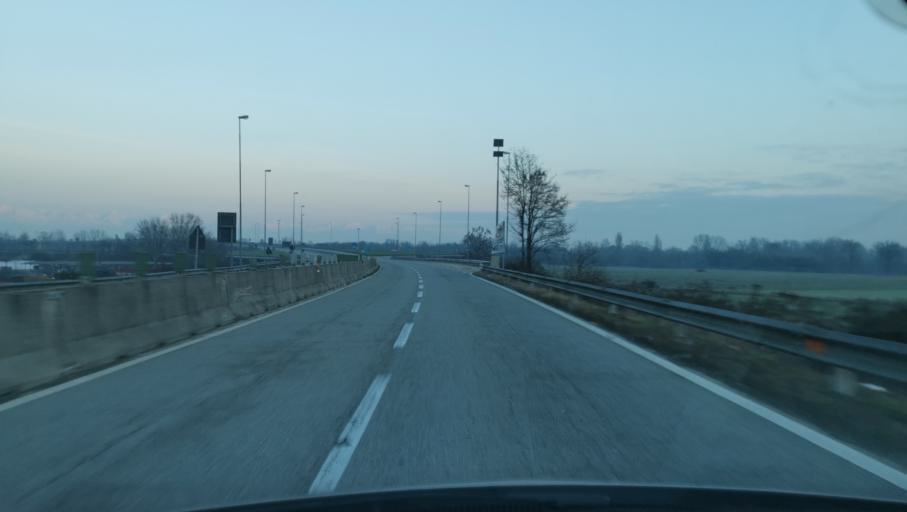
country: IT
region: Piedmont
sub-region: Provincia di Torino
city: Brandizzo
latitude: 45.1831
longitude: 7.8595
